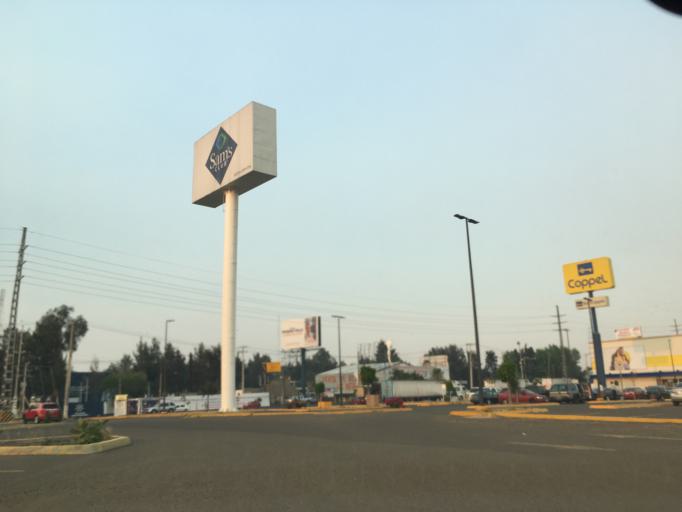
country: MX
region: Michoacan
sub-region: Morelia
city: Morelos
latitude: 19.6775
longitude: -101.2338
